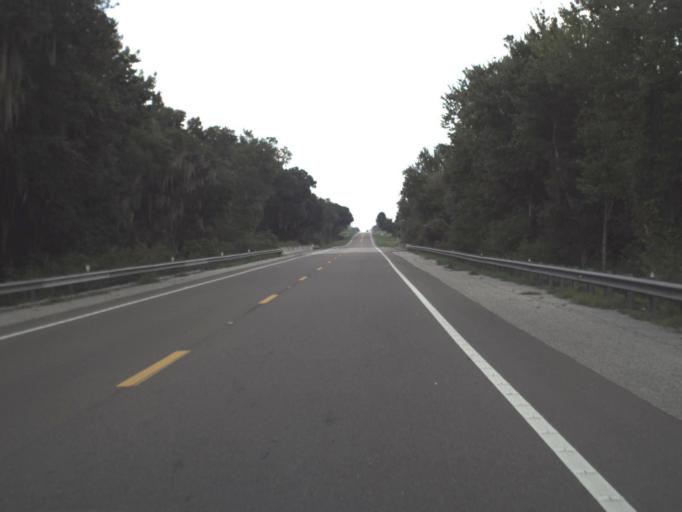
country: US
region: Florida
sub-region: Hillsborough County
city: Balm
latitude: 27.7046
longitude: -82.1843
